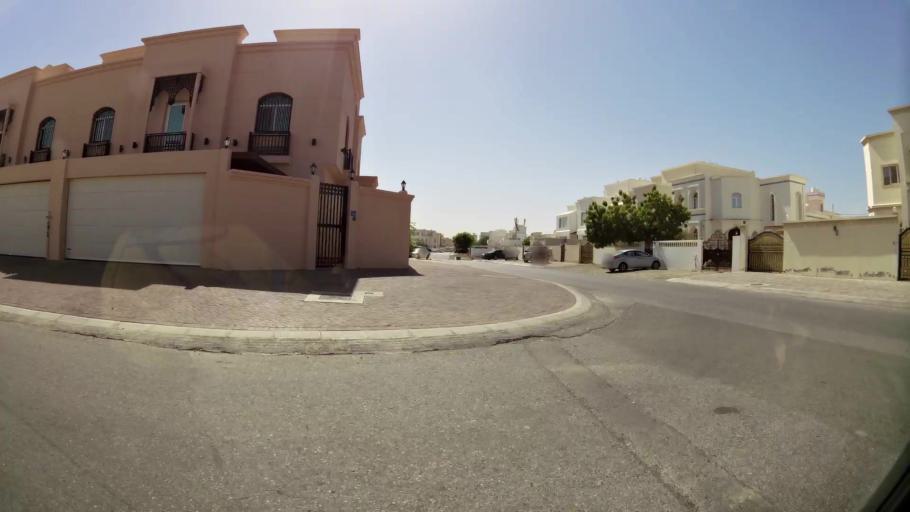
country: OM
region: Muhafazat Masqat
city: As Sib al Jadidah
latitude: 23.6083
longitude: 58.2382
